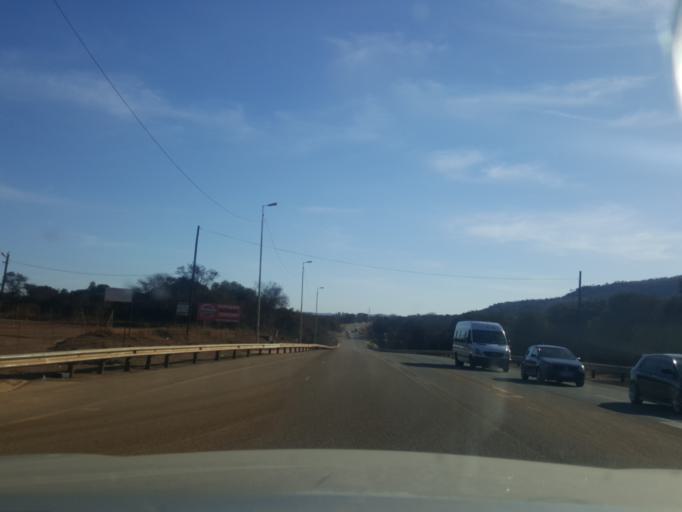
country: ZA
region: North-West
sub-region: Ngaka Modiri Molema District Municipality
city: Zeerust
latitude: -25.5418
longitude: 26.1068
